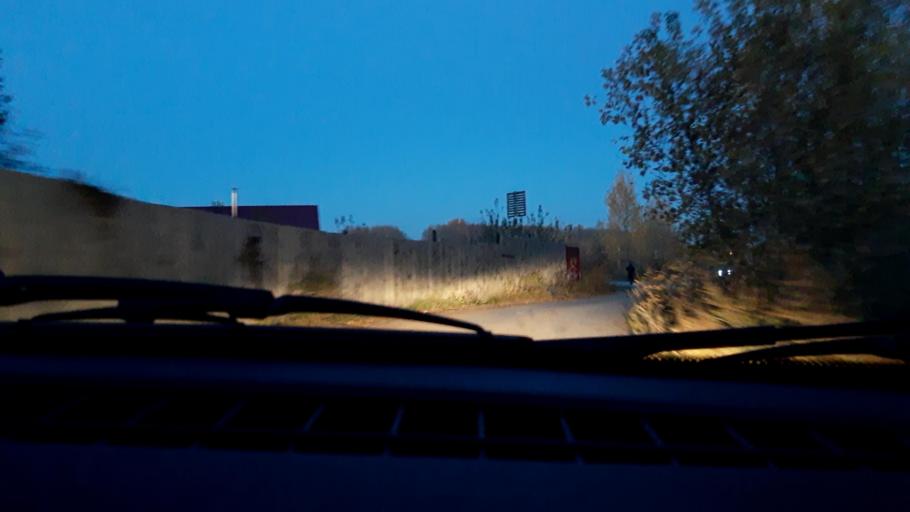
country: RU
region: Bashkortostan
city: Mikhaylovka
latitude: 54.7572
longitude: 55.9081
